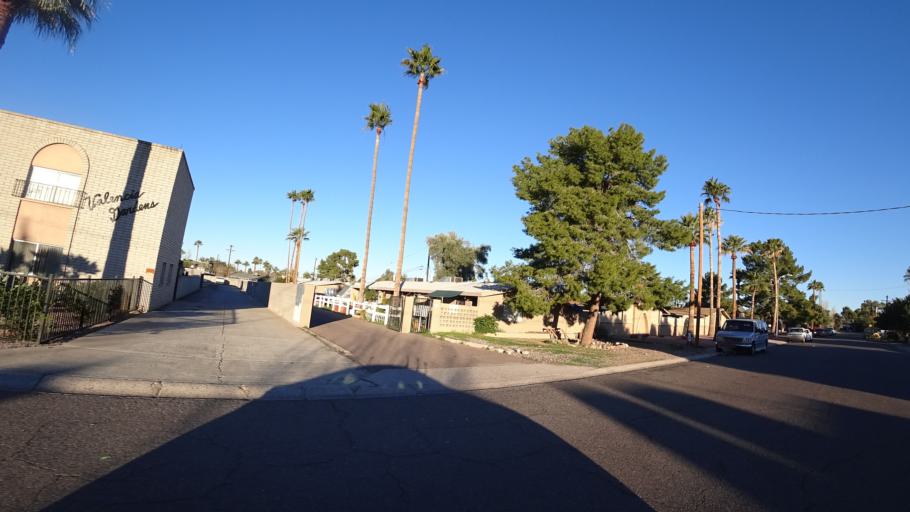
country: US
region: Arizona
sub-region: Maricopa County
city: Paradise Valley
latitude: 33.4889
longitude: -112.0020
